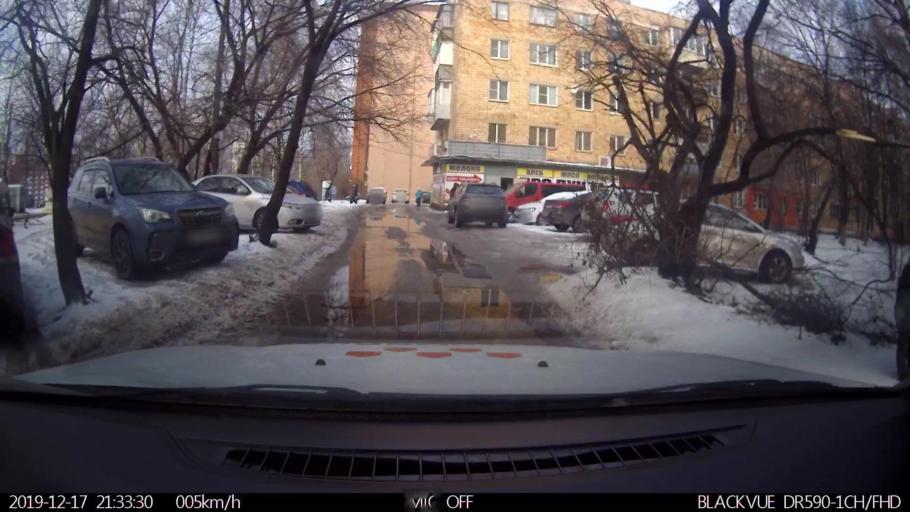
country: RU
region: Nizjnij Novgorod
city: Bor
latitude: 56.3113
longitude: 44.0752
